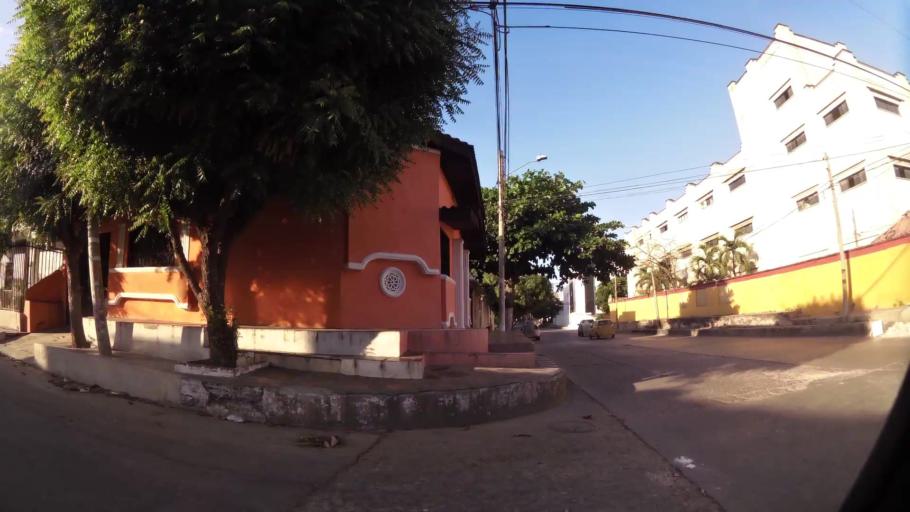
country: CO
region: Atlantico
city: Barranquilla
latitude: 10.9819
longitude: -74.7924
